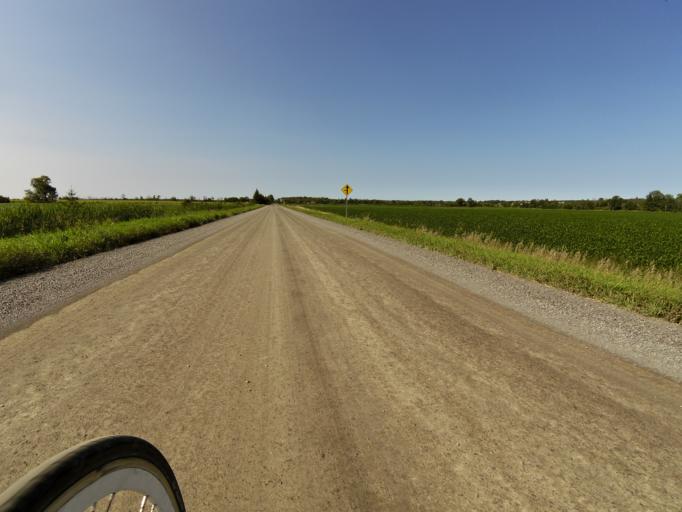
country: CA
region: Ontario
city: Arnprior
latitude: 45.3781
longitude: -76.1478
